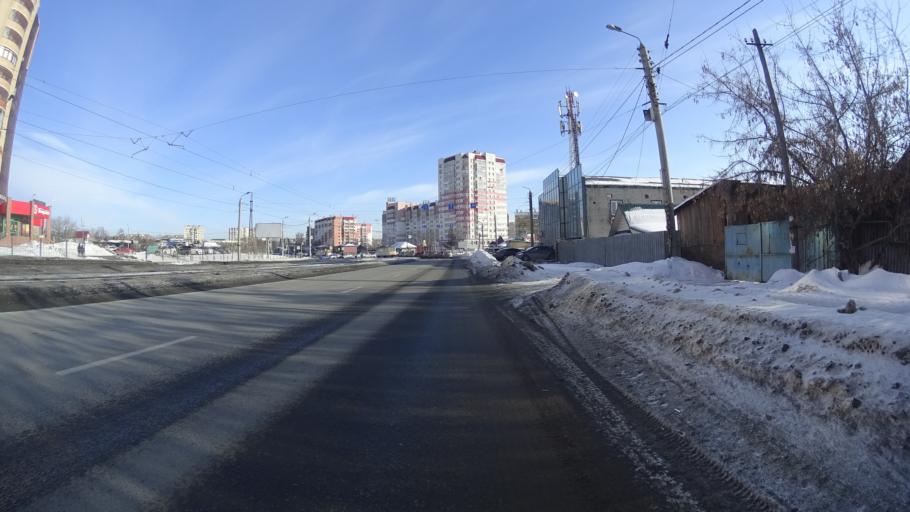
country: RU
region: Chelyabinsk
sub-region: Gorod Chelyabinsk
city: Chelyabinsk
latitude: 55.1843
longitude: 61.3695
